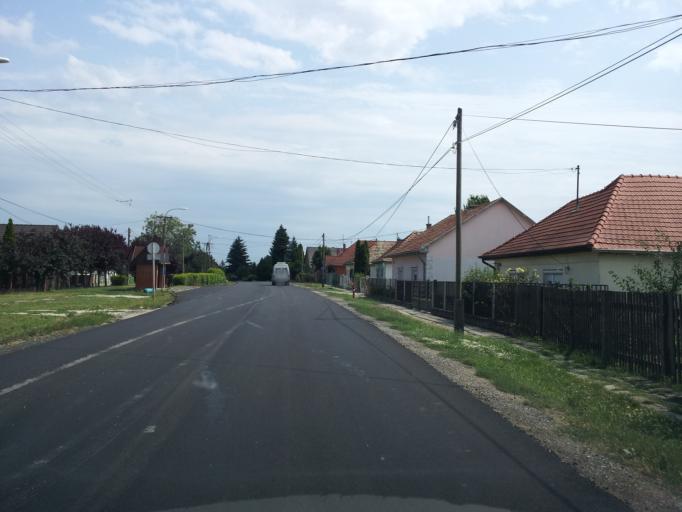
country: HU
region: Fejer
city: Enying
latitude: 46.9571
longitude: 18.2165
